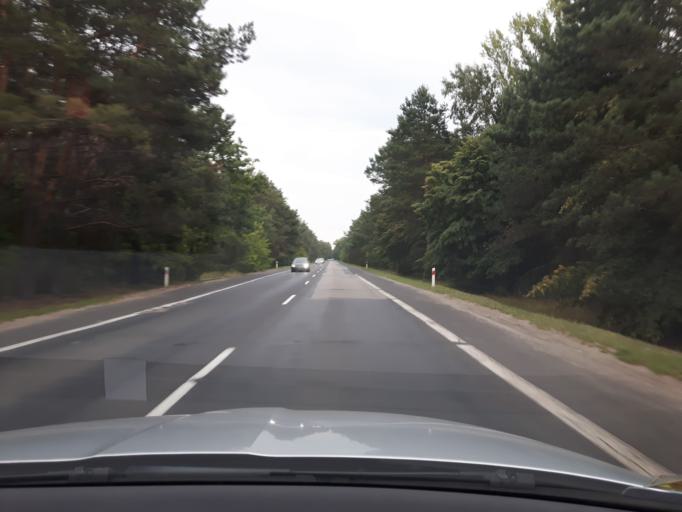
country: PL
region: Masovian Voivodeship
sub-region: Powiat legionowski
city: Bialobrzegi
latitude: 52.4214
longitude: 21.0577
